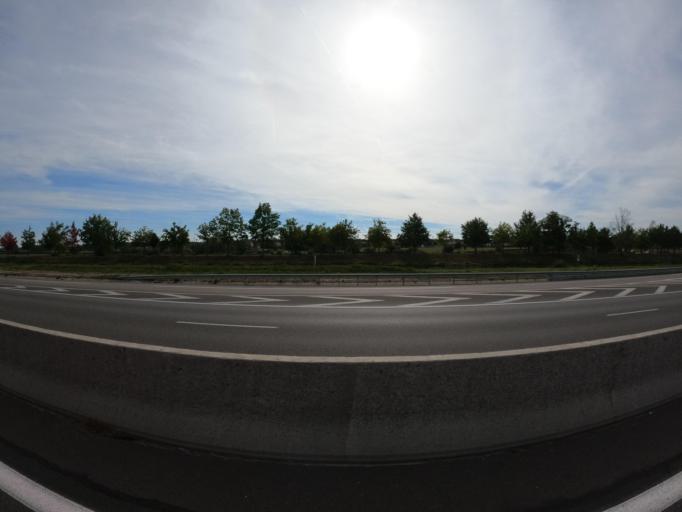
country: FR
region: Bourgogne
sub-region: Departement de Saone-et-Loire
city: Montchanin
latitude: 46.7381
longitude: 4.4823
